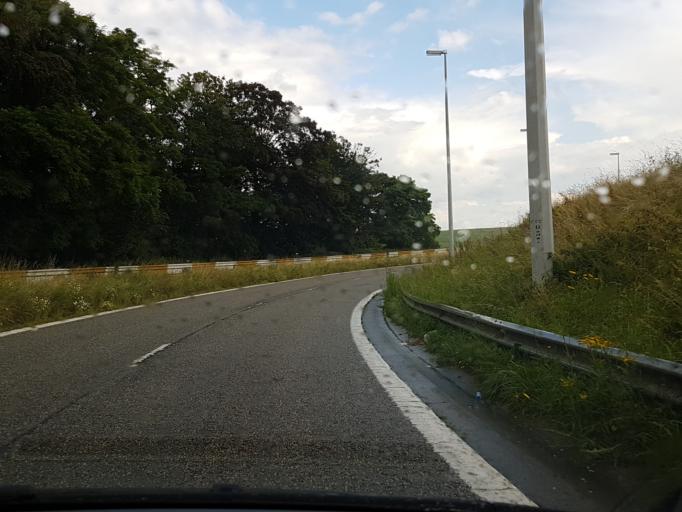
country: BE
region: Flanders
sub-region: Provincie Vlaams-Brabant
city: Bever
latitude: 50.9040
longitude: 4.3255
